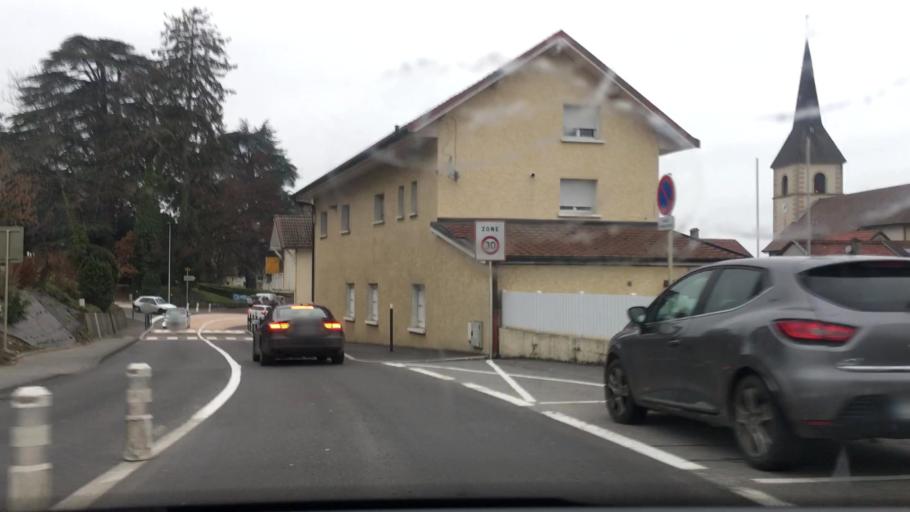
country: FR
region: Rhone-Alpes
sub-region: Departement de la Haute-Savoie
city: Publier
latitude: 46.3874
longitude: 6.5452
